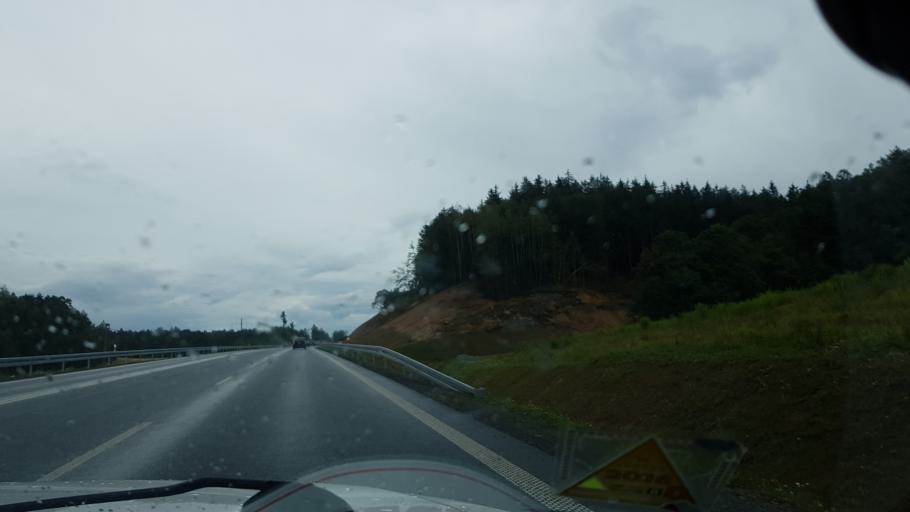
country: PL
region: Lower Silesian Voivodeship
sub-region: Powiat jeleniogorski
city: Myslakowice
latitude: 50.9054
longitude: 15.8123
